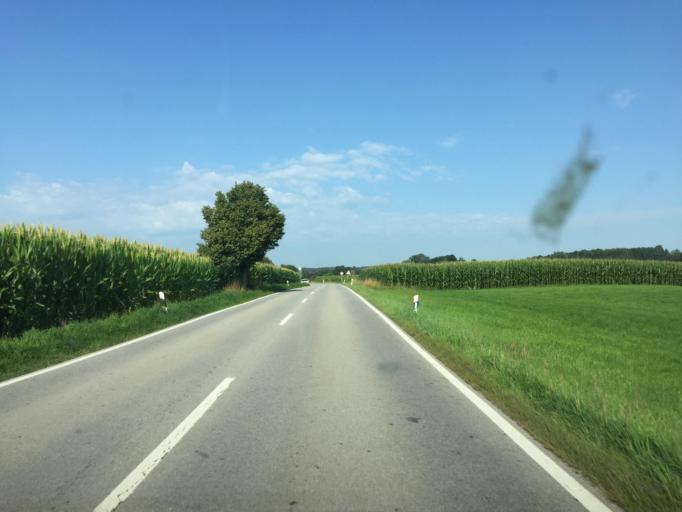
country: DE
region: Bavaria
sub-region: Upper Bavaria
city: Tuntenhausen
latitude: 47.9278
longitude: 11.9981
